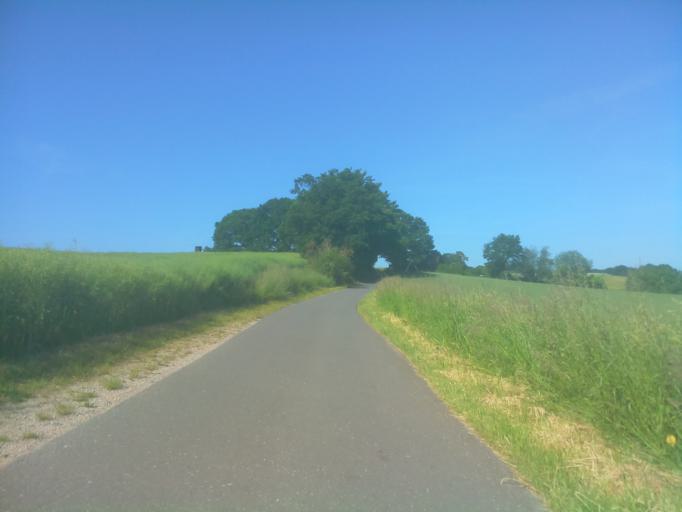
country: DE
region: Thuringia
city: Freienorla
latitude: 50.7677
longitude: 11.5340
